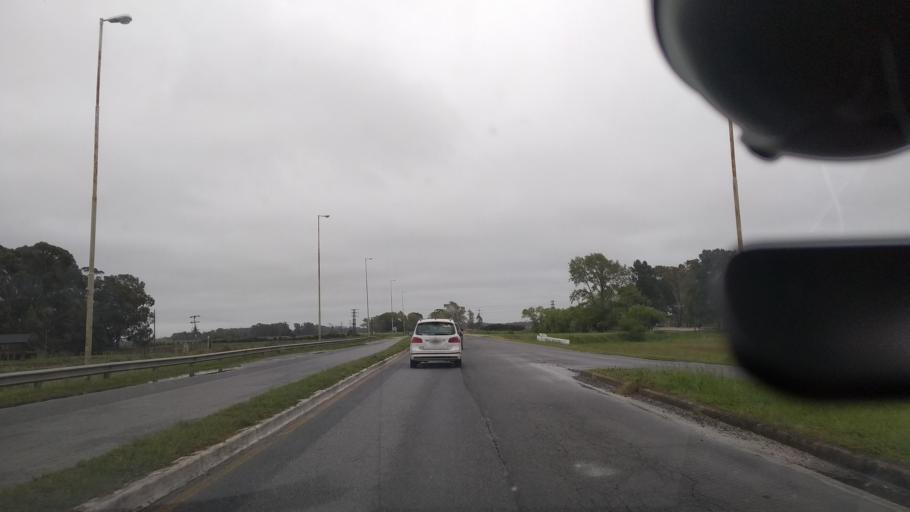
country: AR
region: Buenos Aires
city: Veronica
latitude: -35.3835
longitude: -57.3657
